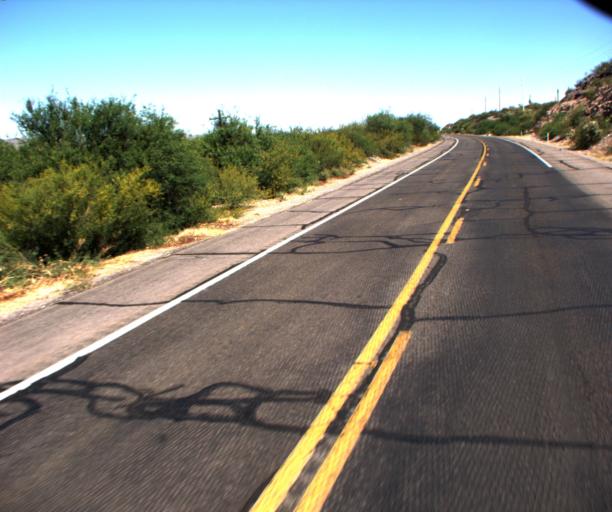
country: US
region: Arizona
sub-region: Pinal County
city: Mammoth
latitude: 32.7530
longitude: -110.6471
